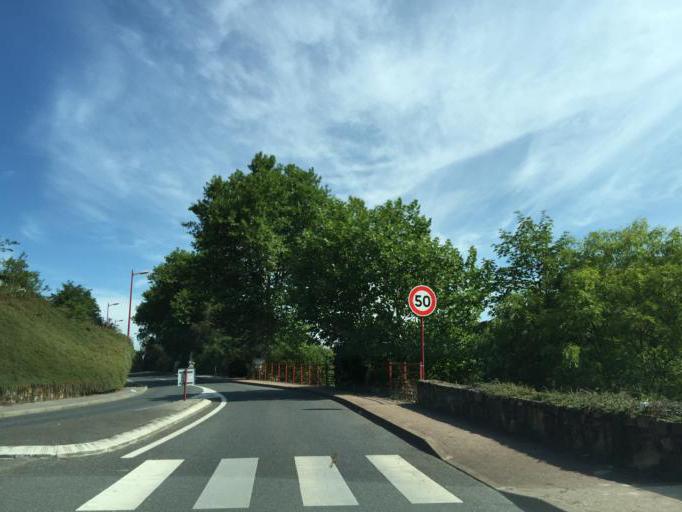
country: FR
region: Midi-Pyrenees
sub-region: Departement de l'Aveyron
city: Le Monastere
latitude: 44.3485
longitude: 2.5824
